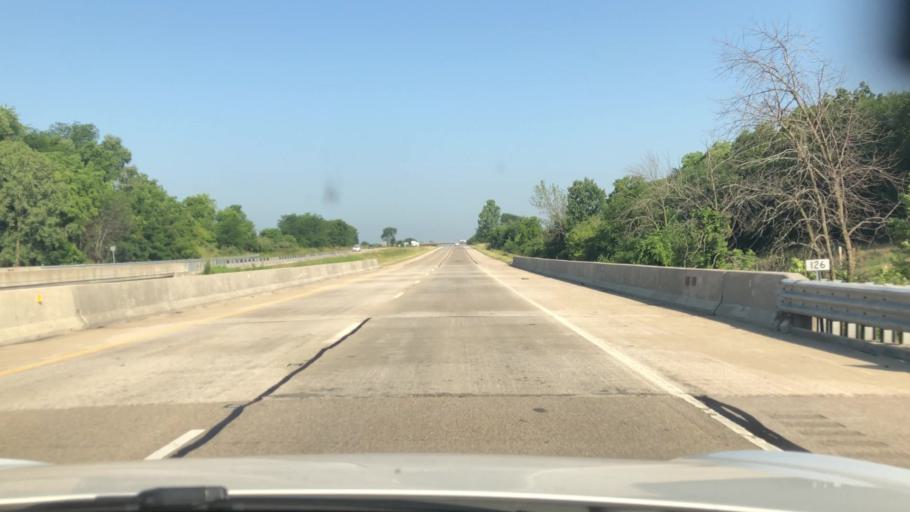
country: US
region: Illinois
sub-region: McLean County
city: Downs
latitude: 40.3966
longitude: -88.8911
